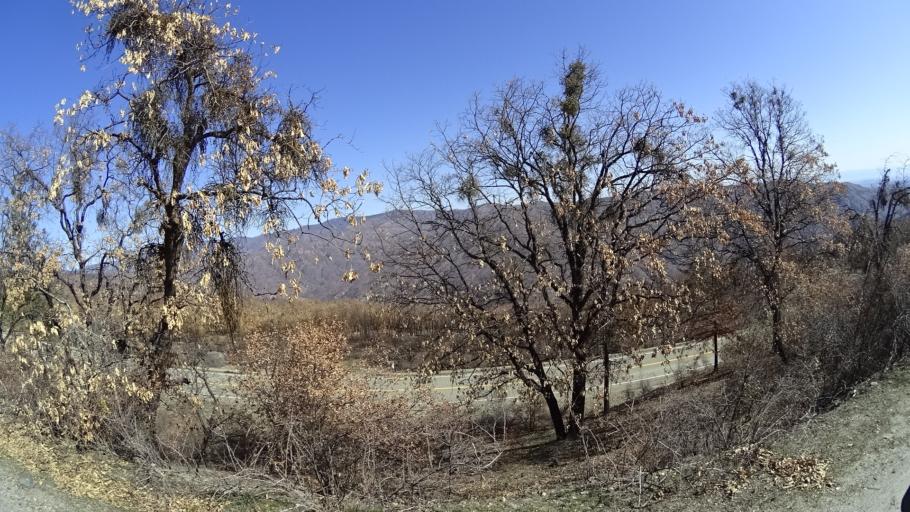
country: US
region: California
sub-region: Tehama County
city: Rancho Tehama Reserve
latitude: 39.6676
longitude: -122.6855
